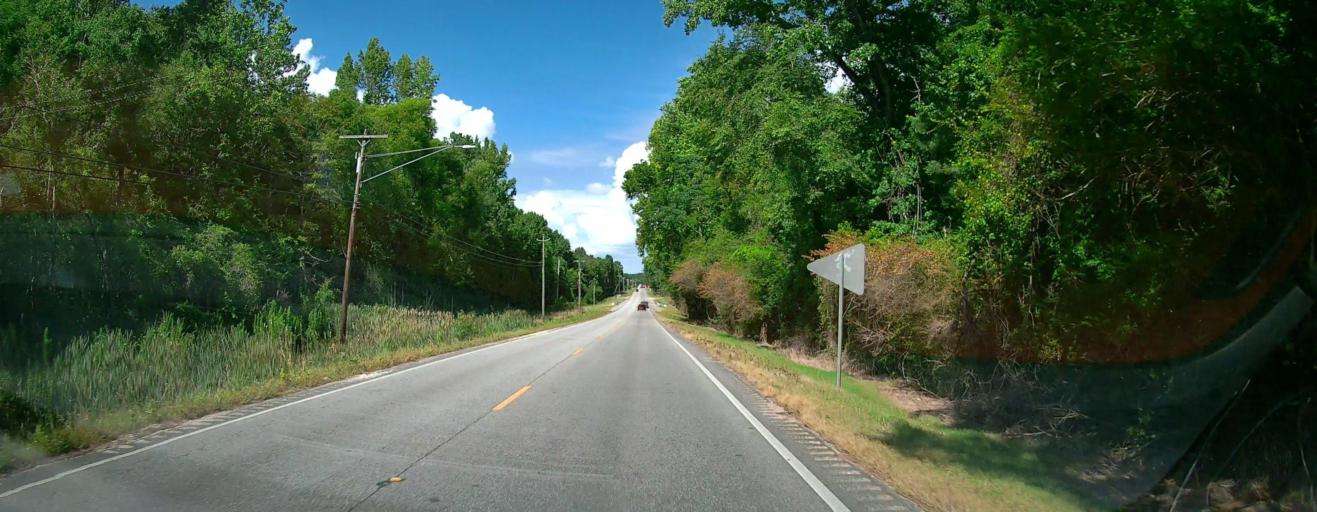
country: US
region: Alabama
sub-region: Macon County
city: Tuskegee
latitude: 32.4334
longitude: -85.6745
